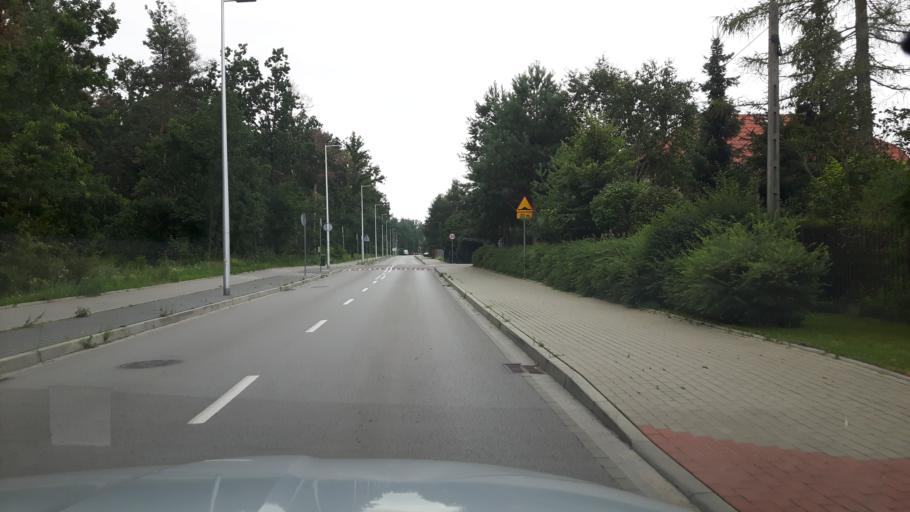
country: PL
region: Masovian Voivodeship
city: Zielonka
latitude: 52.2944
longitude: 21.1626
